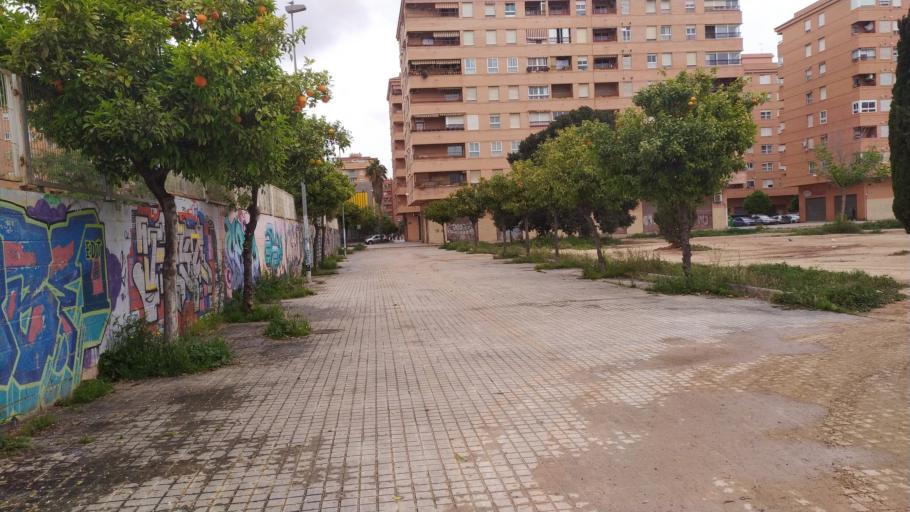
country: ES
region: Valencia
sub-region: Provincia de Valencia
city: Mislata
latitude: 39.4661
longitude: -0.4124
